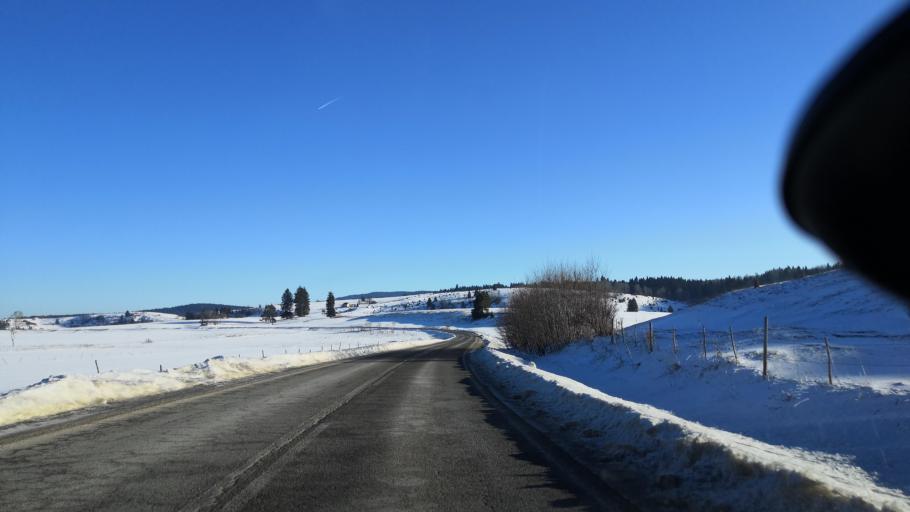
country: BA
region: Republika Srpska
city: Han Pijesak
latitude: 44.0325
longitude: 18.9160
